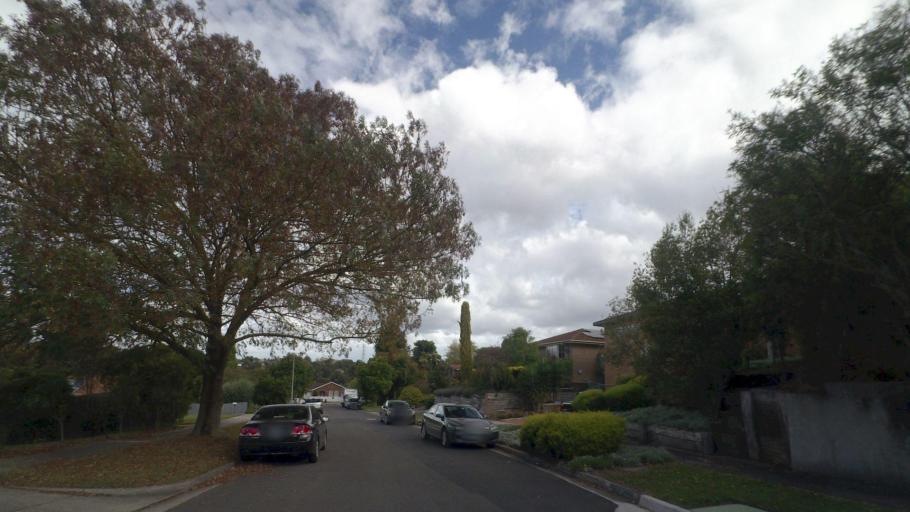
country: AU
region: Victoria
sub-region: Nillumbik
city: Eltham
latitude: -37.7592
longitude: 145.1566
